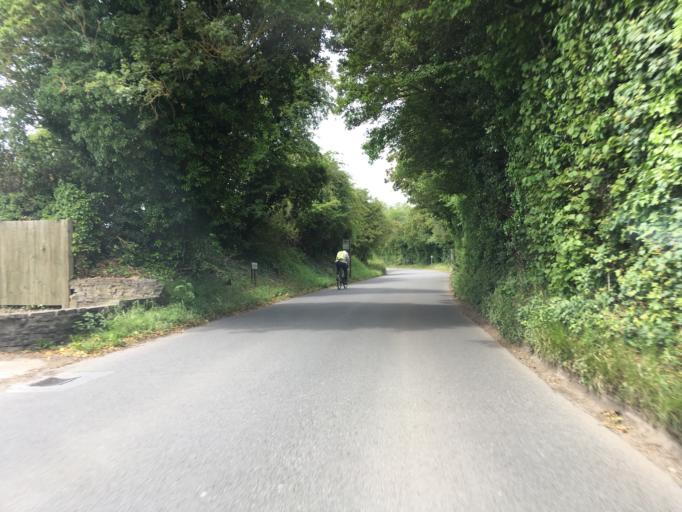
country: GB
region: England
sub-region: Wiltshire
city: Purton
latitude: 51.5685
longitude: -1.8550
